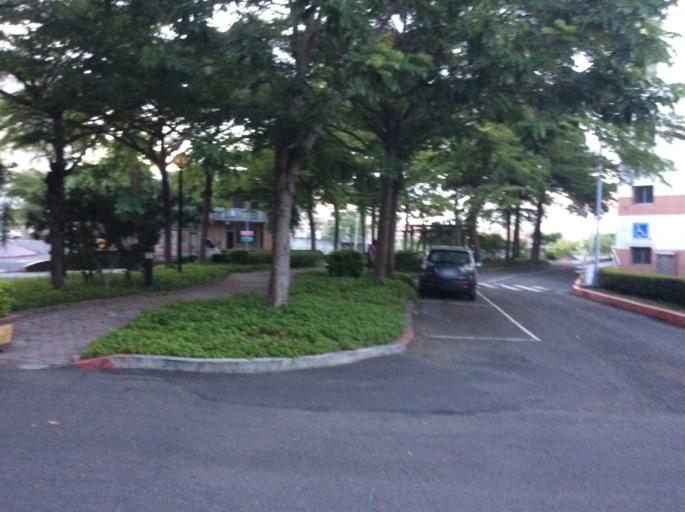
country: TW
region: Kaohsiung
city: Kaohsiung
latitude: 22.6795
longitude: 120.3242
